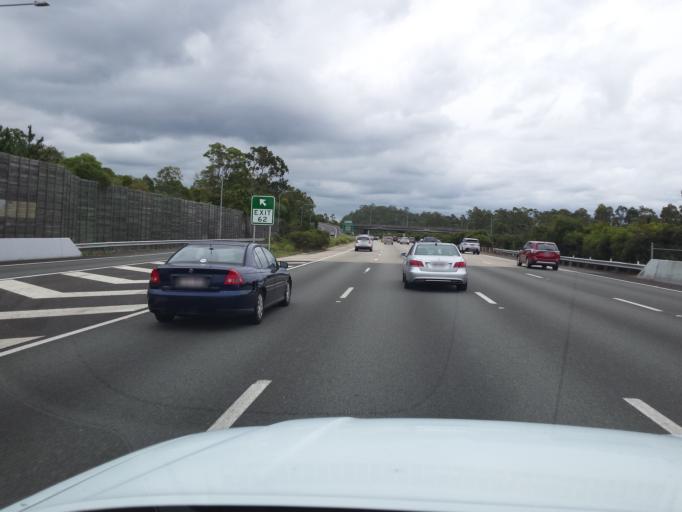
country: AU
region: Queensland
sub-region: Gold Coast
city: Oxenford
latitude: -27.9300
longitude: 153.3325
